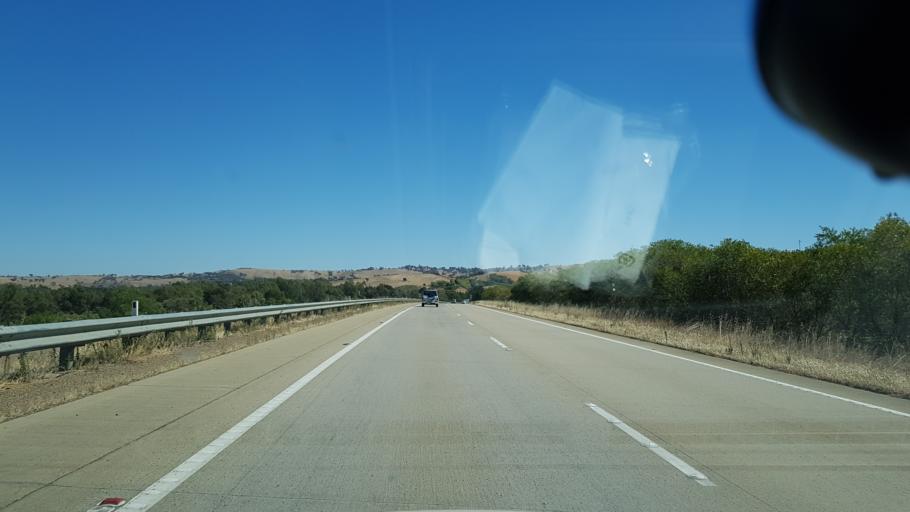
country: AU
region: New South Wales
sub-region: Gundagai
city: Gundagai
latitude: -34.8198
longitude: 148.3662
